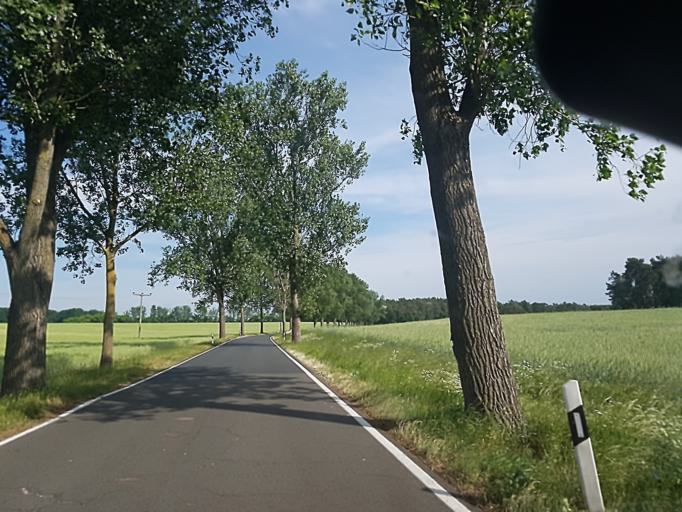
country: DE
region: Saxony-Anhalt
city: Kropstadt
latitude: 51.9727
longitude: 12.7326
